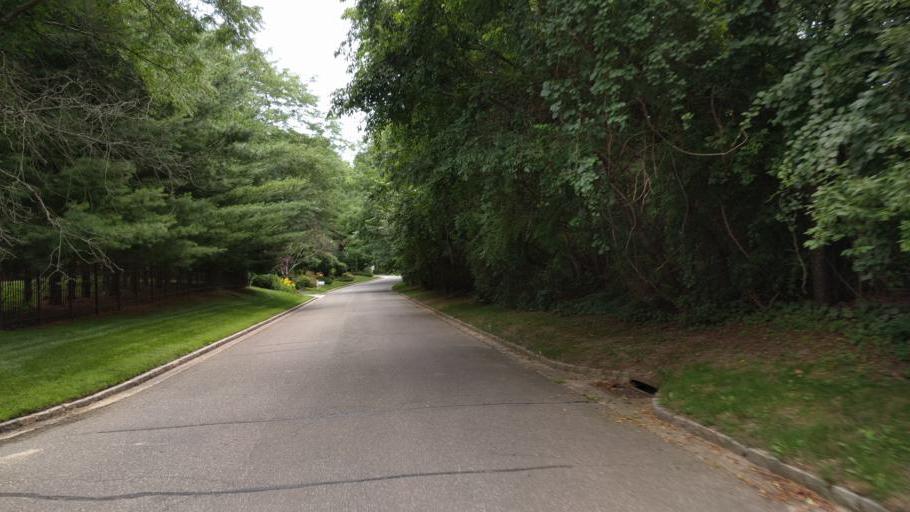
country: US
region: New York
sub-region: Nassau County
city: Muttontown
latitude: 40.8274
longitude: -73.5506
